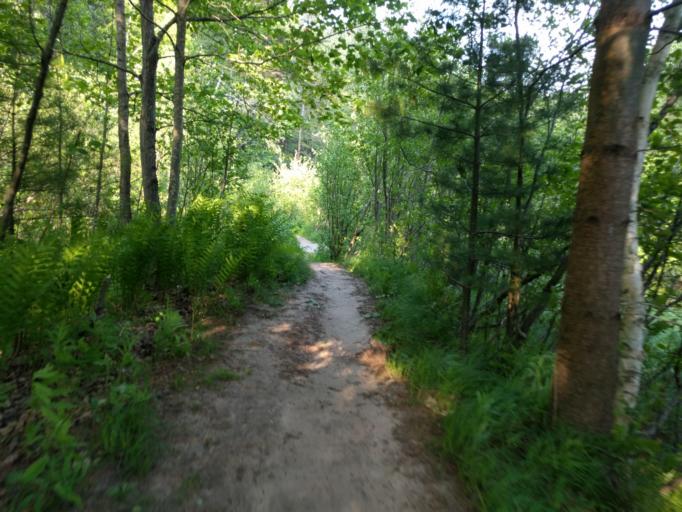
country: US
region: Michigan
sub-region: Marquette County
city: Trowbridge Park
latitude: 46.5686
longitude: -87.4470
